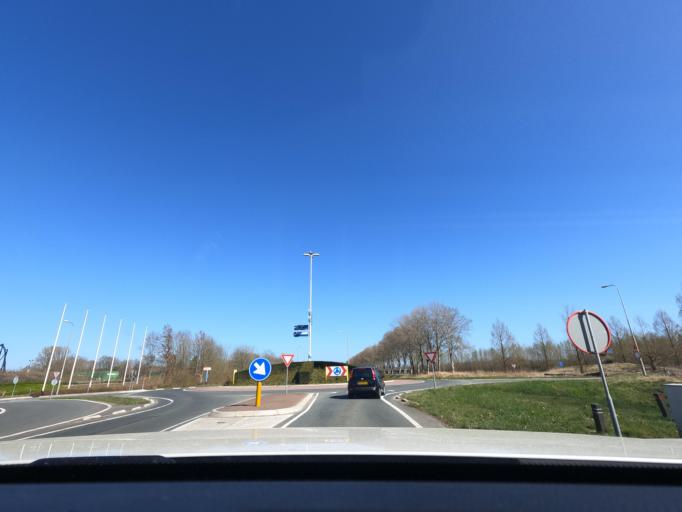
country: NL
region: Gelderland
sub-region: Gemeente Nunspeet
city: Nunspeet
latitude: 52.4344
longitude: 5.7607
